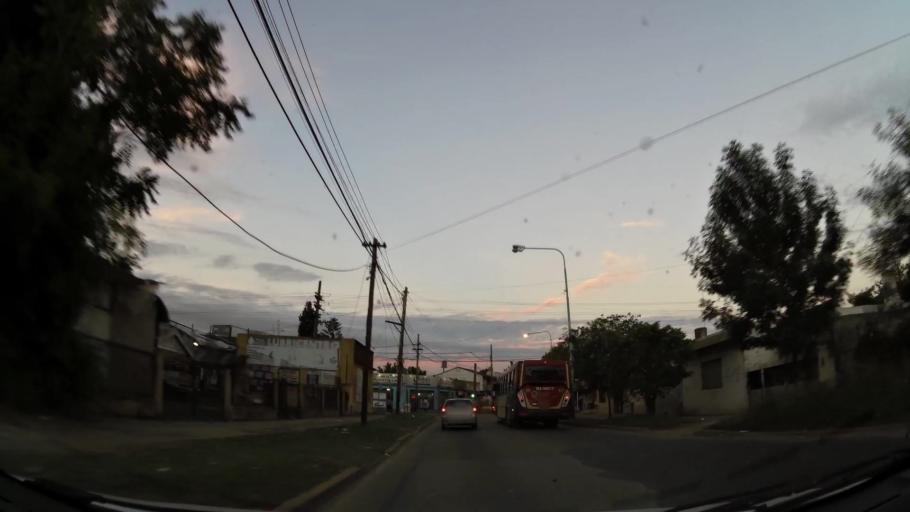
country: AR
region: Buenos Aires
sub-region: Partido de Merlo
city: Merlo
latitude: -34.6670
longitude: -58.7397
